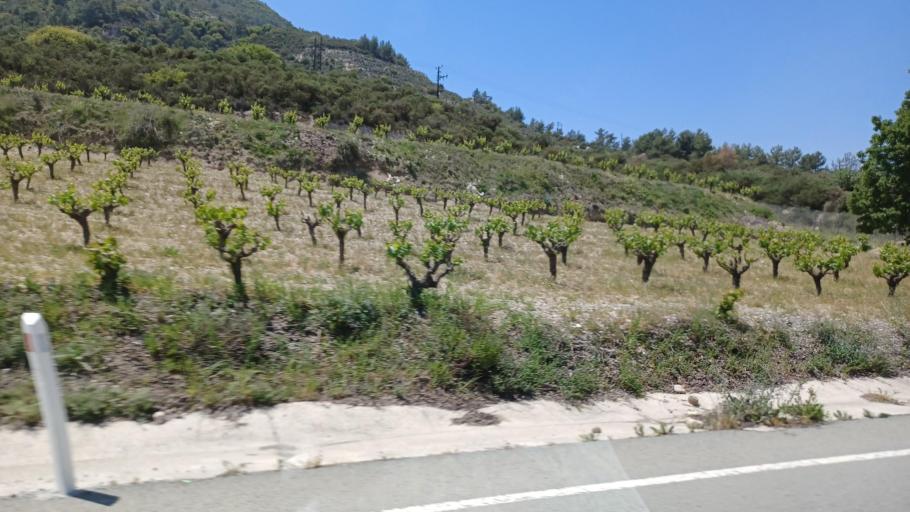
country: CY
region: Limassol
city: Pelendri
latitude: 34.8579
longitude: 32.9318
